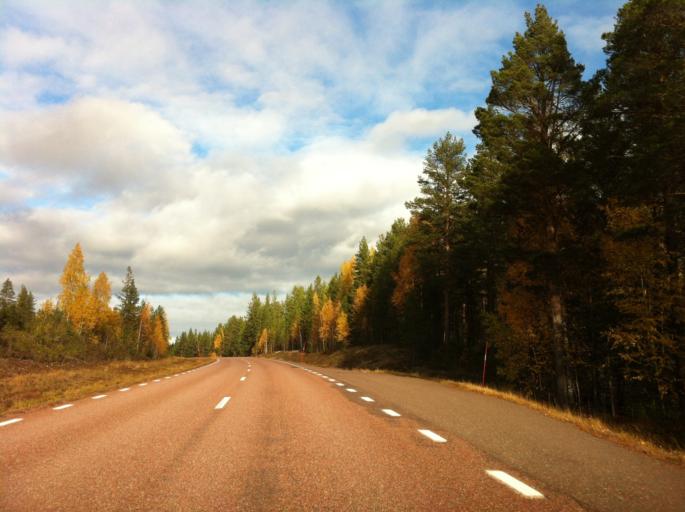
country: SE
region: Dalarna
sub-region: Alvdalens Kommun
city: AElvdalen
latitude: 61.5120
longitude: 13.3737
